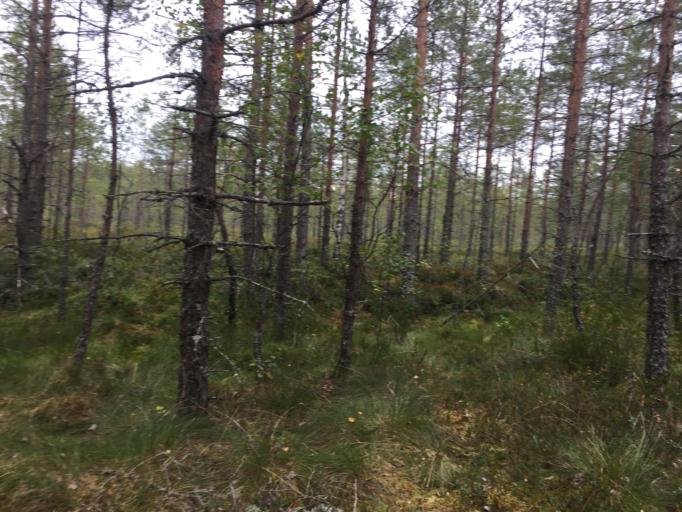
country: RU
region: Leningrad
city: Rozhdestveno
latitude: 59.2907
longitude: 30.0078
